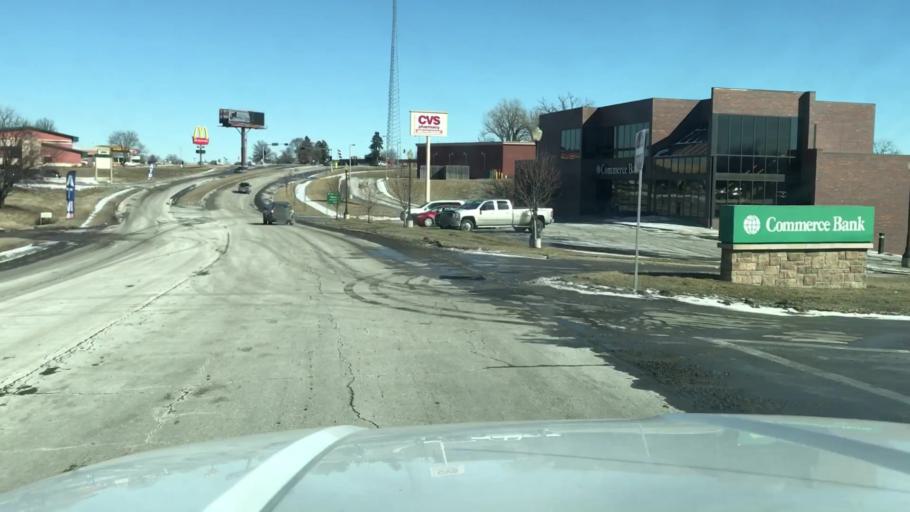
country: US
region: Missouri
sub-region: Andrew County
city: Country Club Village
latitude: 39.7994
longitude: -94.8174
